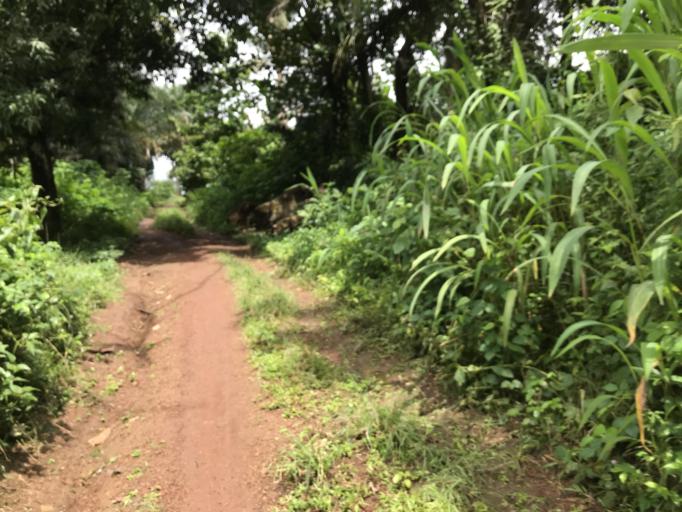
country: SL
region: Eastern Province
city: Buedu
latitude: 8.4707
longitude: -10.3240
